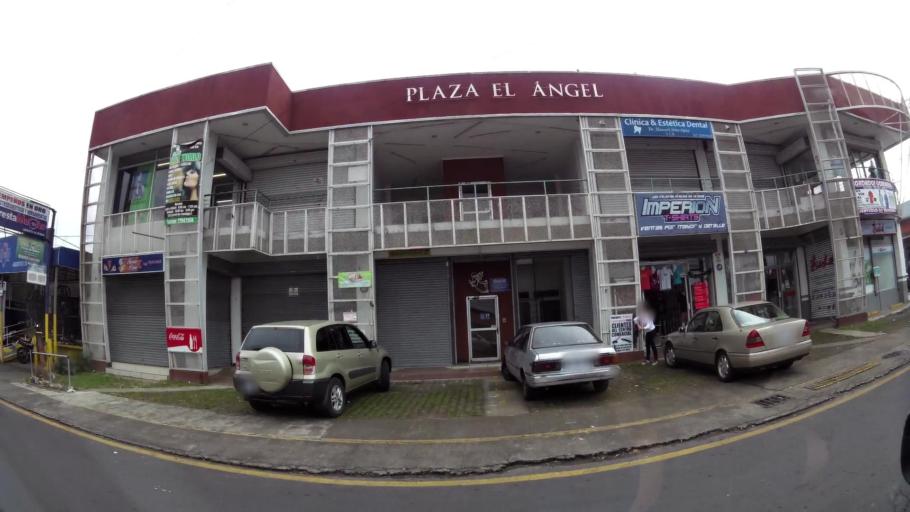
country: CR
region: San Jose
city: Ipis
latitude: 9.9777
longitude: -84.0080
